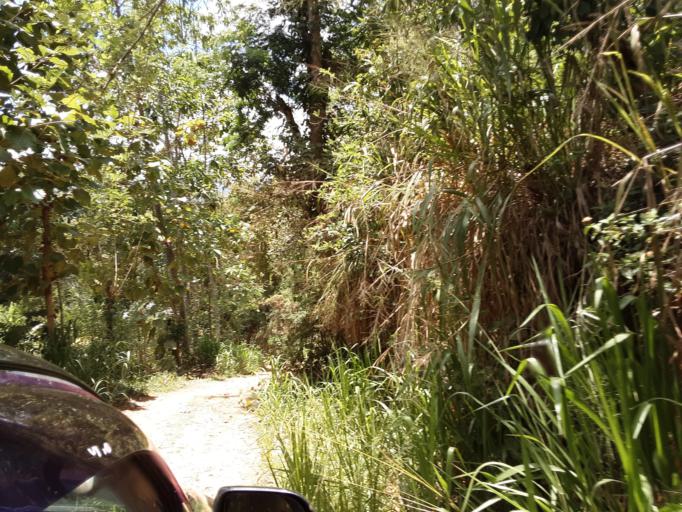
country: LK
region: Uva
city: Haputale
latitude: 6.8124
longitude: 81.1093
